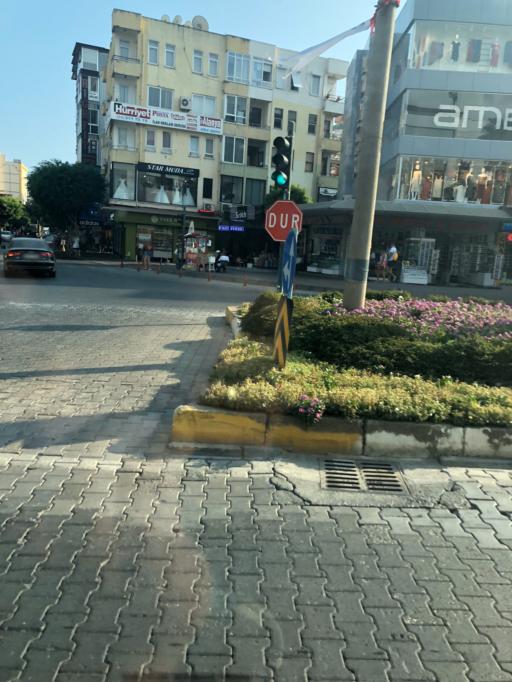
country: TR
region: Antalya
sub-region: Alanya
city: Alanya
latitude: 36.5440
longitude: 31.9975
